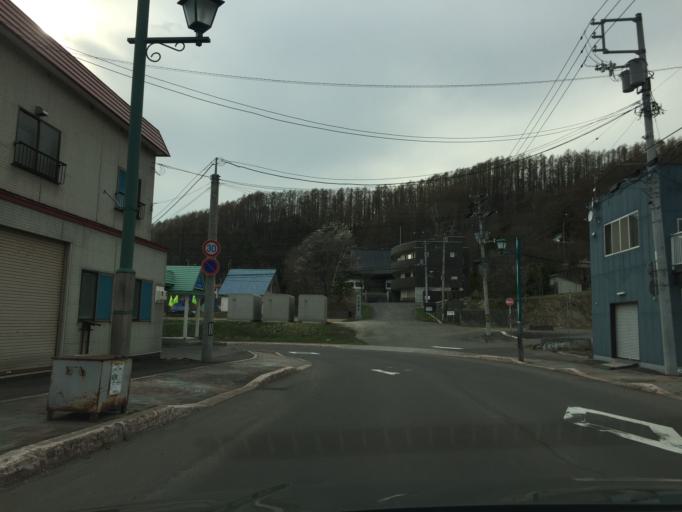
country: JP
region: Hokkaido
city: Utashinai
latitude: 43.5225
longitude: 142.0398
